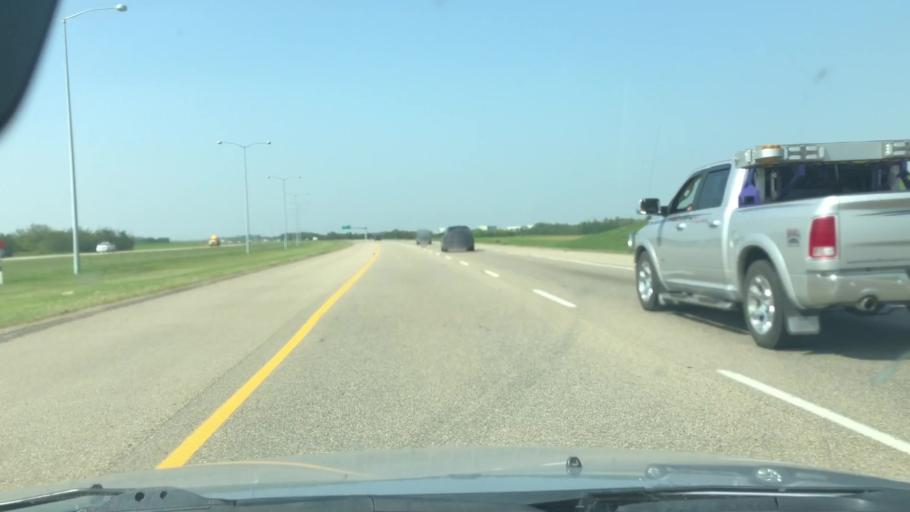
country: CA
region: Alberta
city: Edmonton
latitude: 53.6466
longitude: -113.5171
